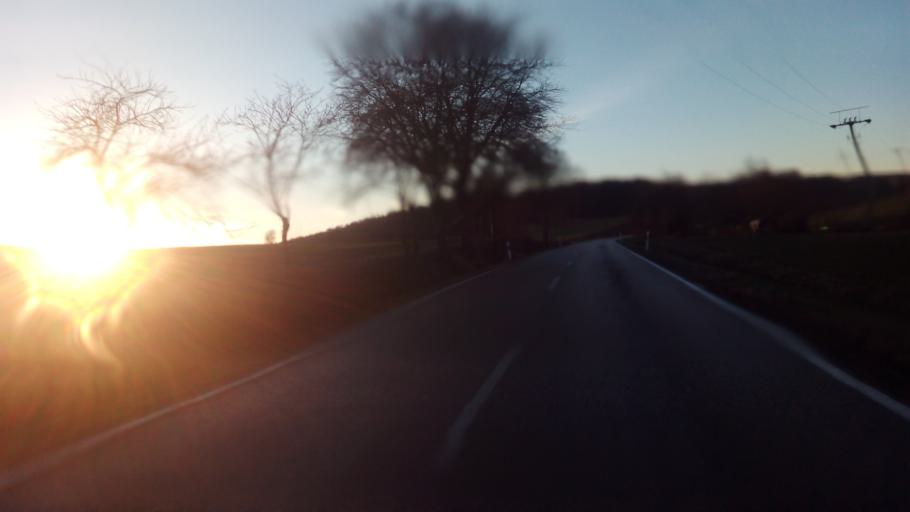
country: DE
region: Baden-Wuerttemberg
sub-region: Tuebingen Region
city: Oberdischingen
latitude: 48.3317
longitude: 9.8465
